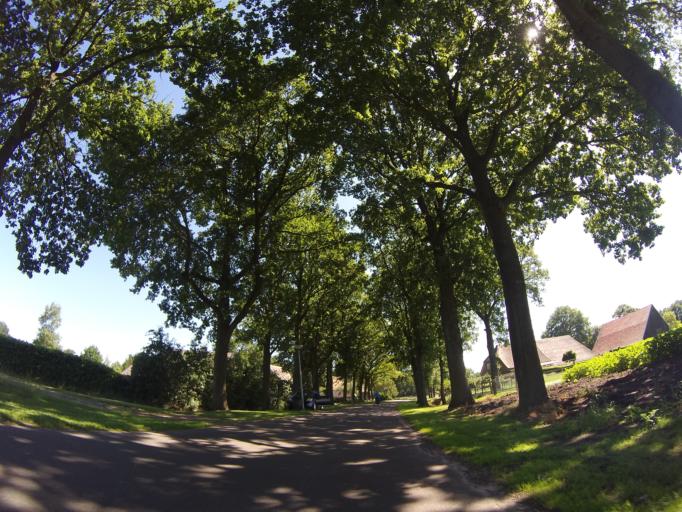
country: NL
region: Drenthe
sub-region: Gemeente Coevorden
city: Sleen
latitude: 52.7949
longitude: 6.8028
